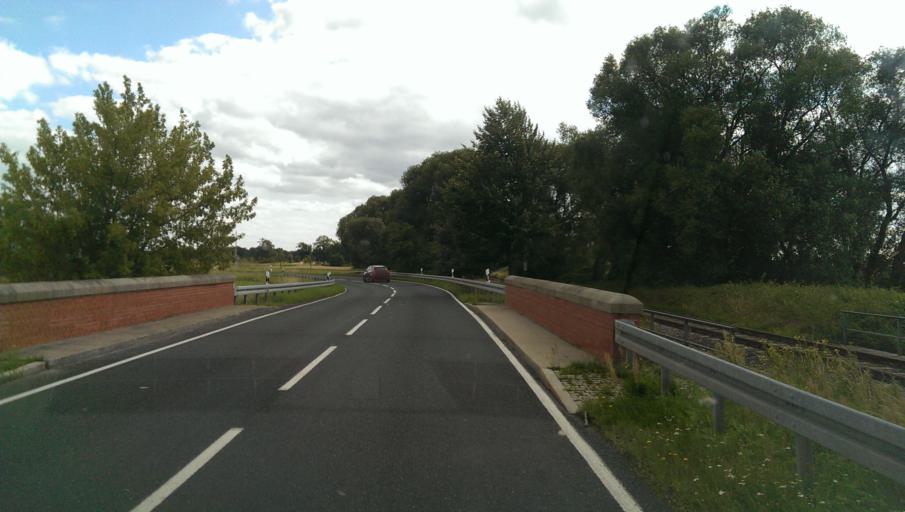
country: DE
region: Saxony-Anhalt
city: Oranienbaum
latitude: 51.8187
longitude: 12.4069
